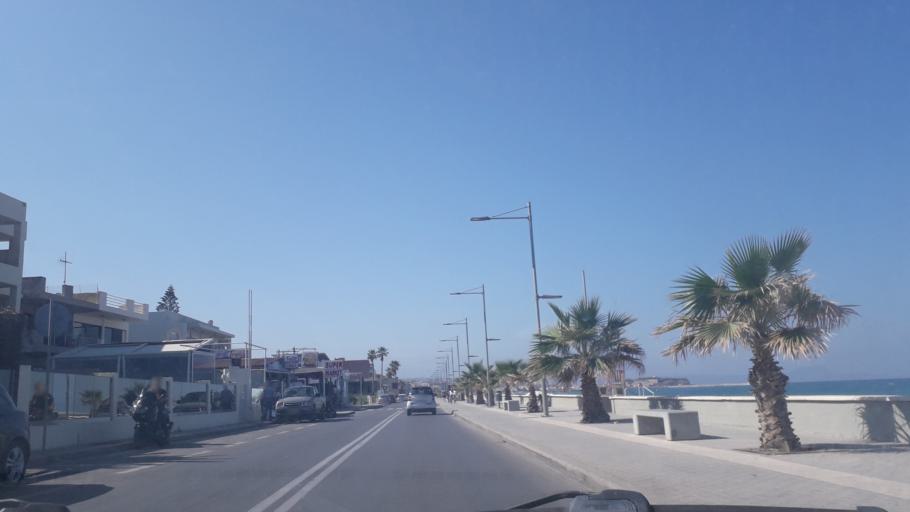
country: GR
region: Crete
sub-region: Nomos Rethymnis
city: Rethymno
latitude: 35.3682
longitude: 24.5042
